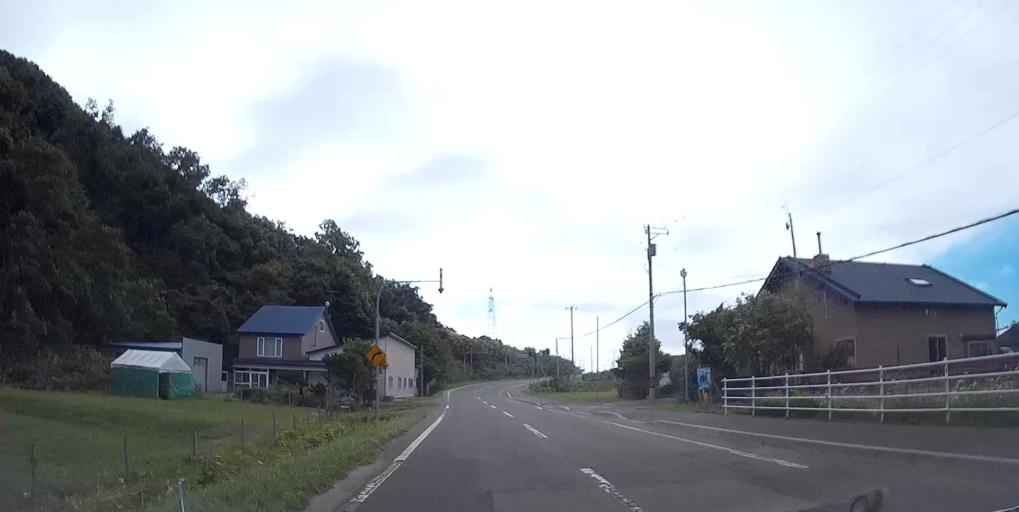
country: JP
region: Hokkaido
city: Kamiiso
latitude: 41.9716
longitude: 140.1480
